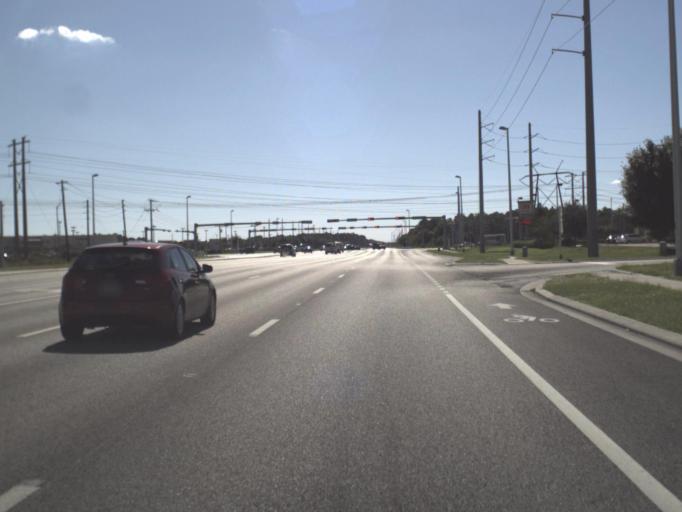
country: US
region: Florida
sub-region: Lee County
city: Gateway
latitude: 26.6201
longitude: -81.7698
